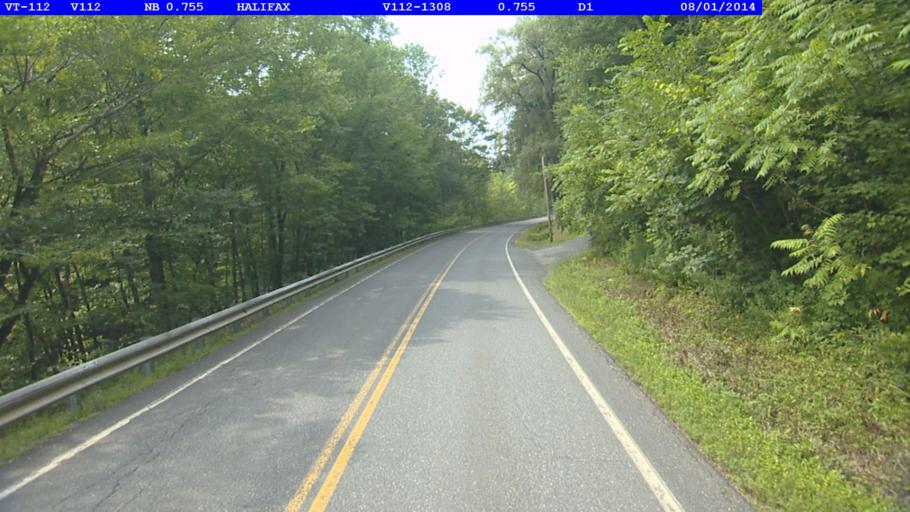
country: US
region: Massachusetts
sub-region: Franklin County
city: Colrain
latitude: 42.7416
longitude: -72.7317
